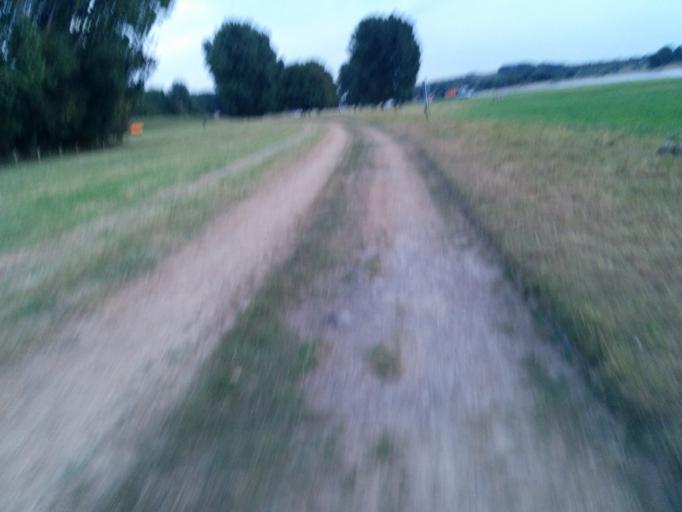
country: DE
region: North Rhine-Westphalia
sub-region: Regierungsbezirk Dusseldorf
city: Hochfeld
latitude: 51.4365
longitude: 6.7166
